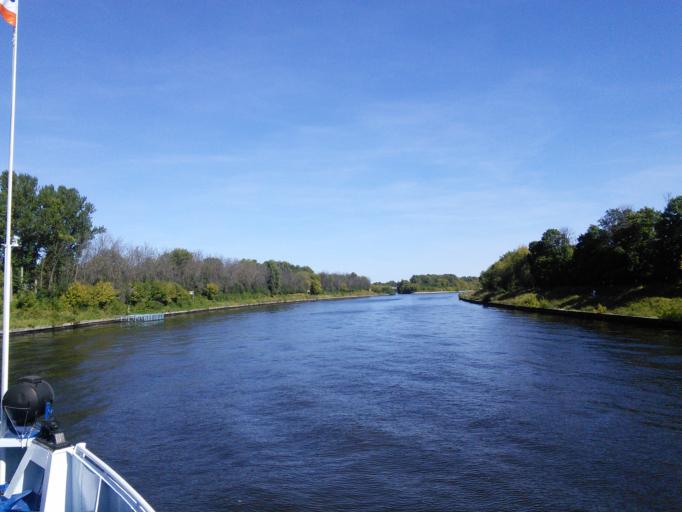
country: RU
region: Moskovskaya
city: Dolgoprudnyy
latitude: 55.9518
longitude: 37.4813
